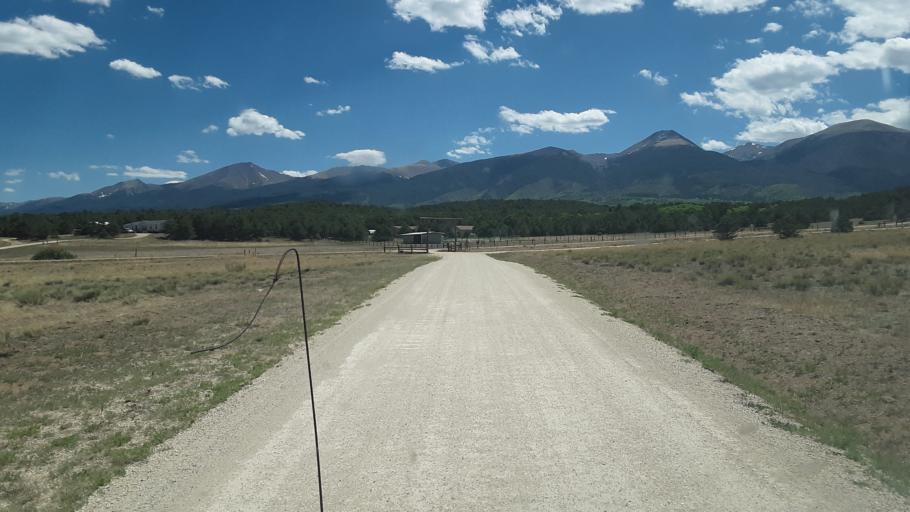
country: US
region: Colorado
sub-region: Custer County
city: Westcliffe
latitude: 38.3104
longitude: -105.6346
